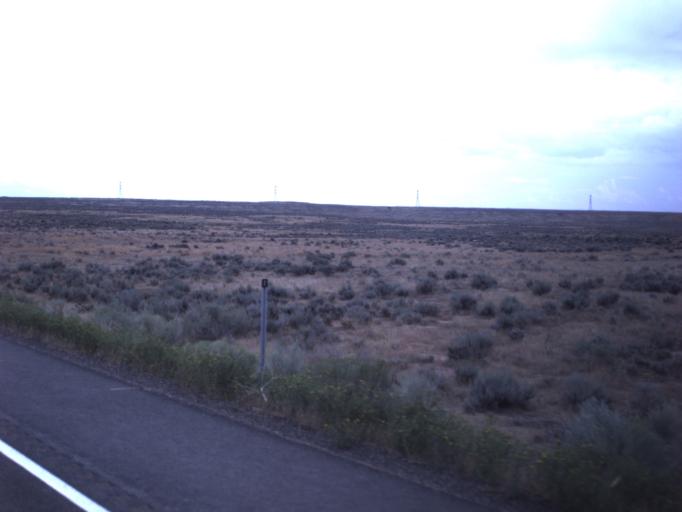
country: US
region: Utah
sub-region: Uintah County
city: Naples
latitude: 40.2480
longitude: -109.4224
